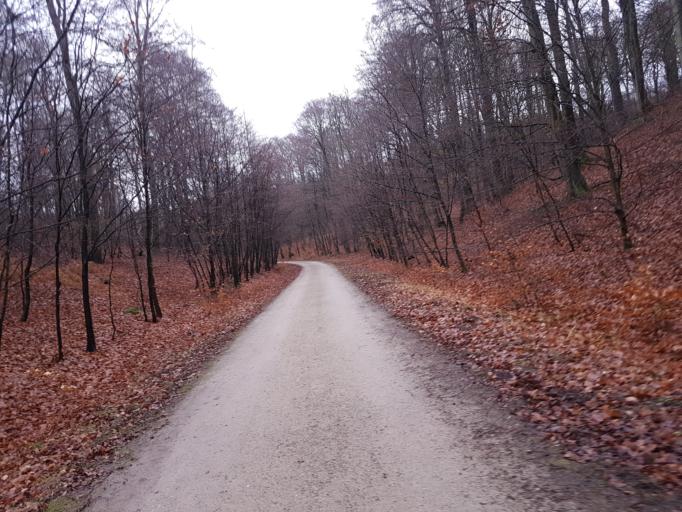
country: DE
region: Mecklenburg-Vorpommern
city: Ostseebad Binz
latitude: 54.3904
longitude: 13.6355
